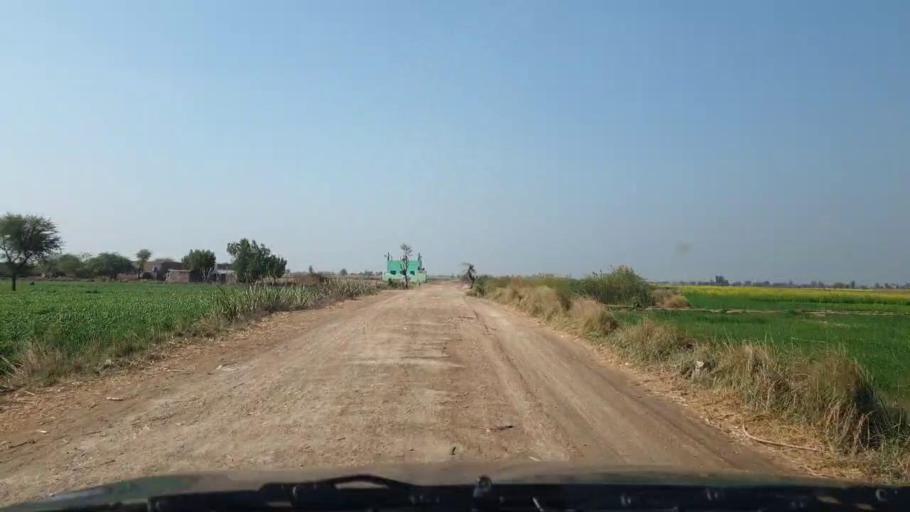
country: PK
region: Sindh
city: Sinjhoro
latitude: 26.0460
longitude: 68.7514
